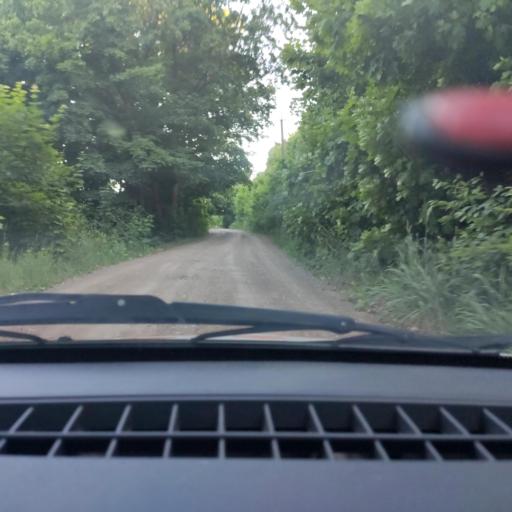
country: RU
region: Bashkortostan
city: Karmaskaly
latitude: 54.3737
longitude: 55.9110
